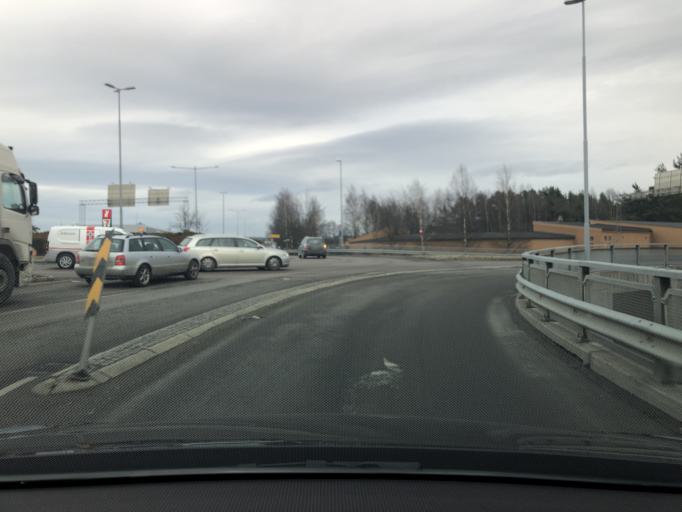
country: NO
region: Akershus
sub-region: Lorenskog
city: Kjenn
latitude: 59.9319
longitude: 10.8599
